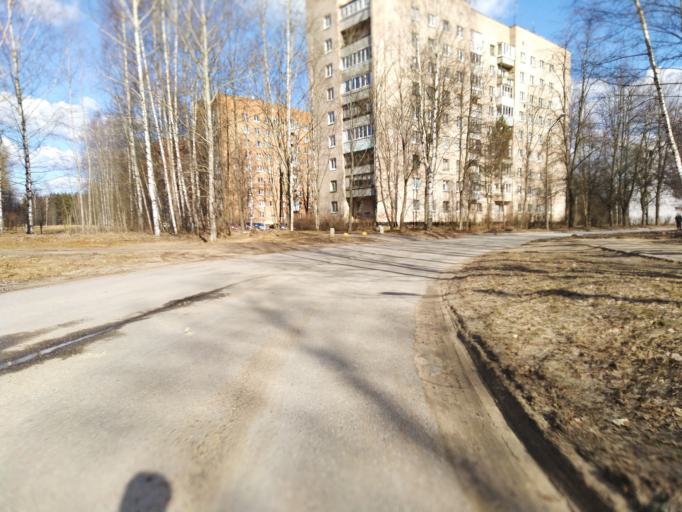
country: RU
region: Leningrad
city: Novoye Devyatkino
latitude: 60.1082
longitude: 30.4827
